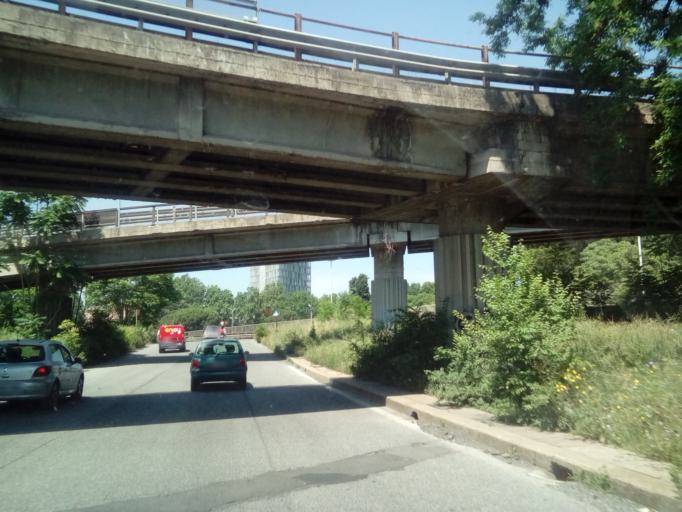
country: IT
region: Latium
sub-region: Citta metropolitana di Roma Capitale
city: Rome
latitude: 41.9085
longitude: 12.5303
